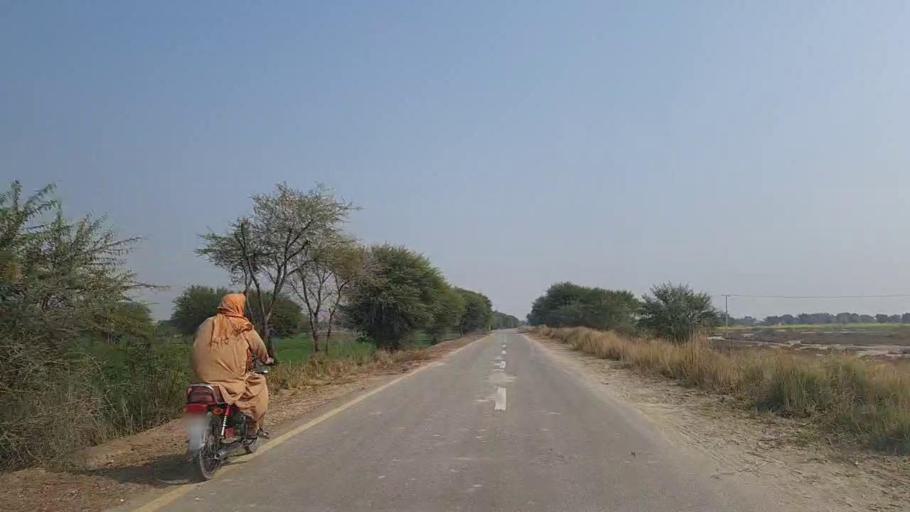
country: PK
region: Sindh
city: Jam Sahib
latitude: 26.3726
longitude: 68.5101
